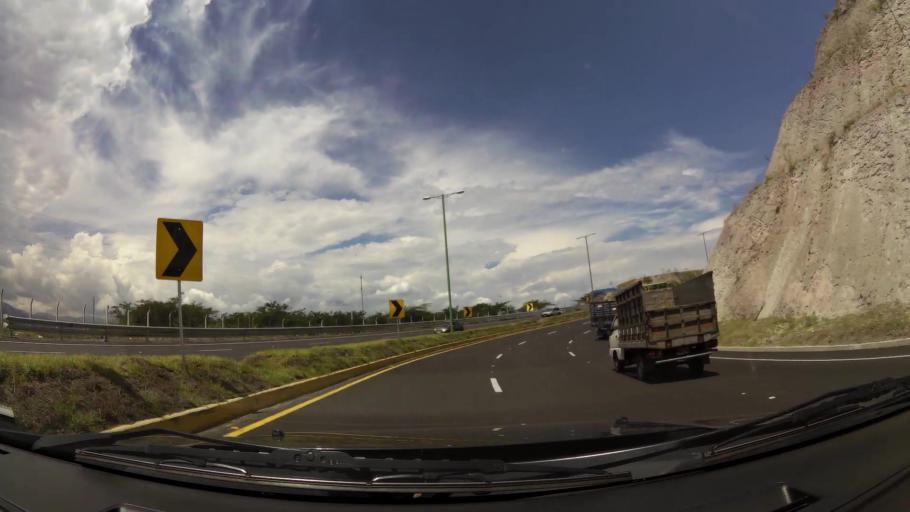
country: EC
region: Pichincha
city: Quito
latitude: -0.0915
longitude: -78.4027
